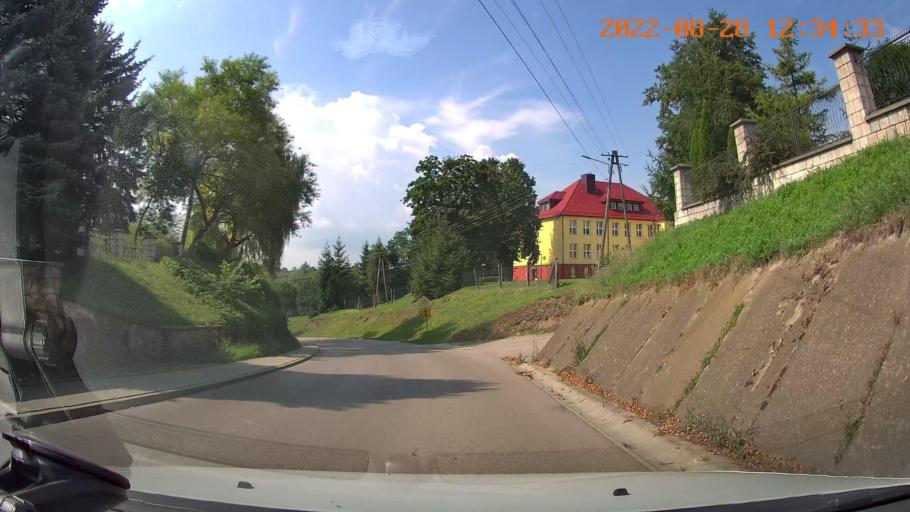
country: PL
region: Swietokrzyskie
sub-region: Powiat kazimierski
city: Skalbmierz
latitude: 50.3775
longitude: 20.4298
